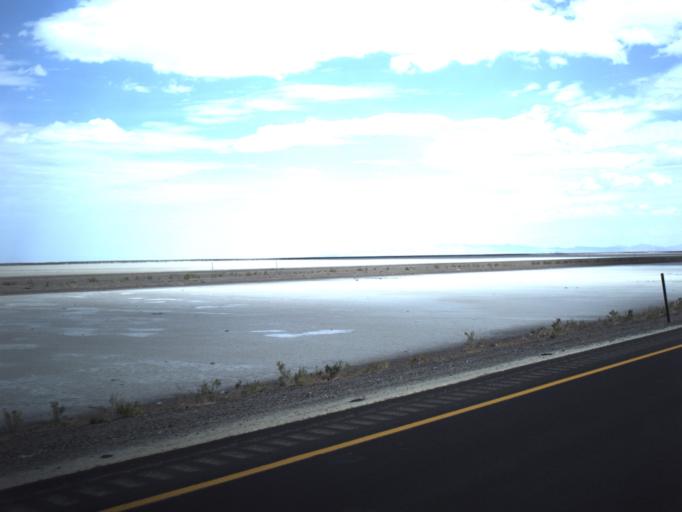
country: US
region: Utah
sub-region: Tooele County
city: Wendover
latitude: 40.7324
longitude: -113.5676
